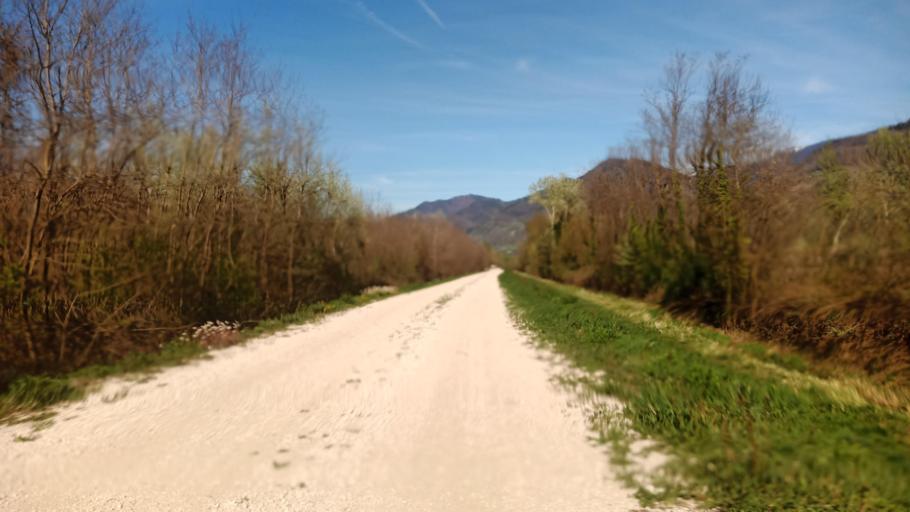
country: FR
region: Rhone-Alpes
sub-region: Departement de l'Isere
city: Froges
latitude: 45.2890
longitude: 5.9229
